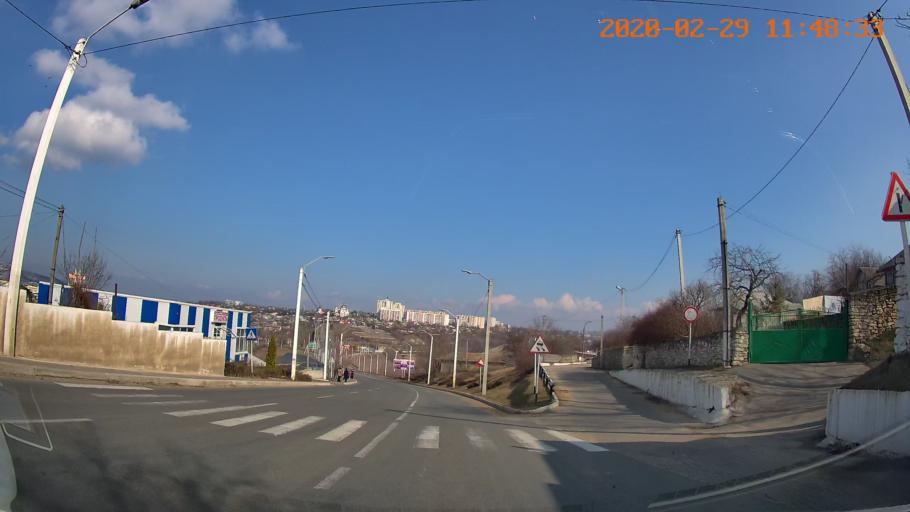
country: MD
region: Rezina
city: Rezina
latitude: 47.7486
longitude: 28.9911
